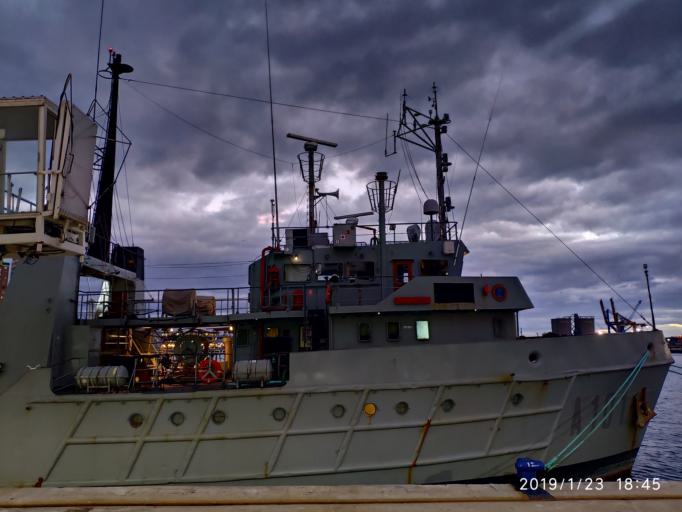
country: ES
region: Andalusia
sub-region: Provincia de Malaga
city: Malaga
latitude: 36.7178
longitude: -4.4167
